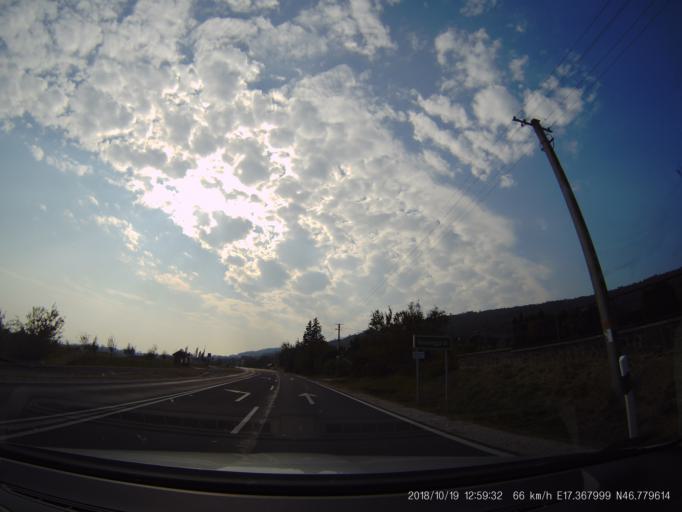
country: HU
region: Zala
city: Vonyarcvashegy
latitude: 46.7796
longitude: 17.3680
